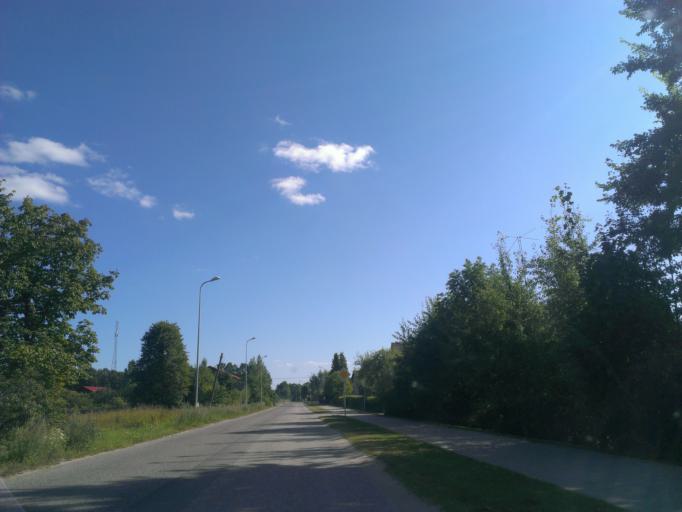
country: LV
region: Sigulda
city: Sigulda
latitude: 57.1611
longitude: 24.8883
